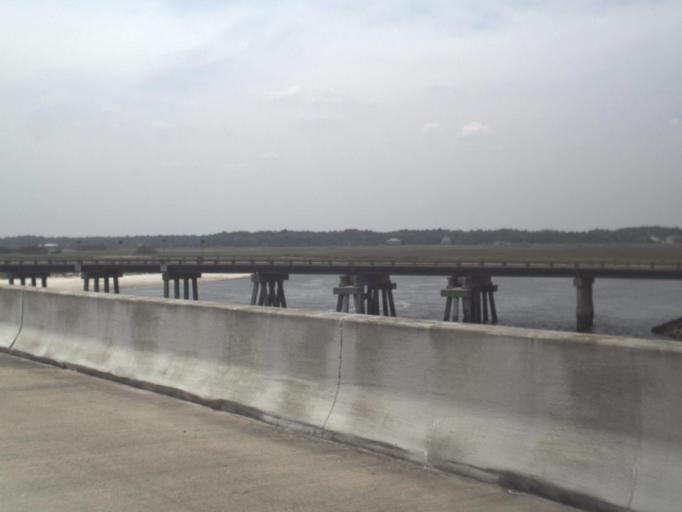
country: US
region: Florida
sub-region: Nassau County
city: Fernandina Beach
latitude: 30.5138
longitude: -81.4557
